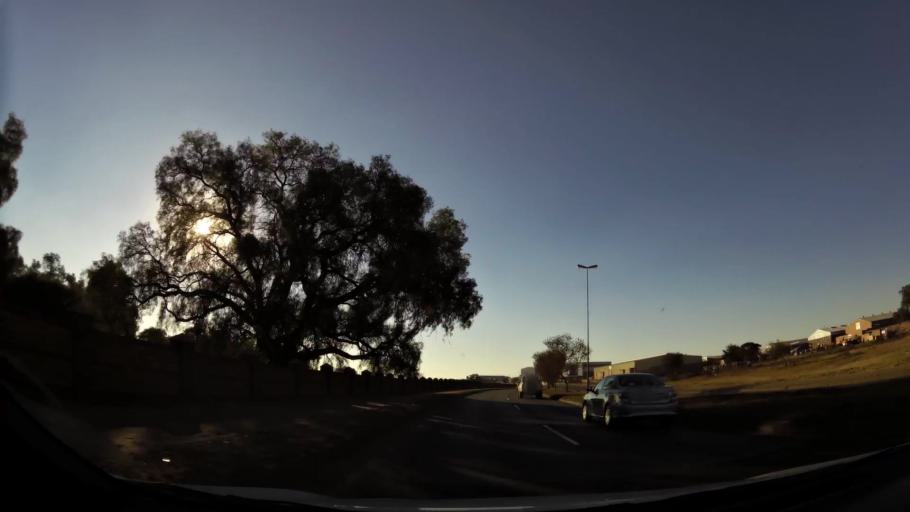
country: ZA
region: Limpopo
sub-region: Capricorn District Municipality
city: Polokwane
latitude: -23.8961
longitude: 29.4382
